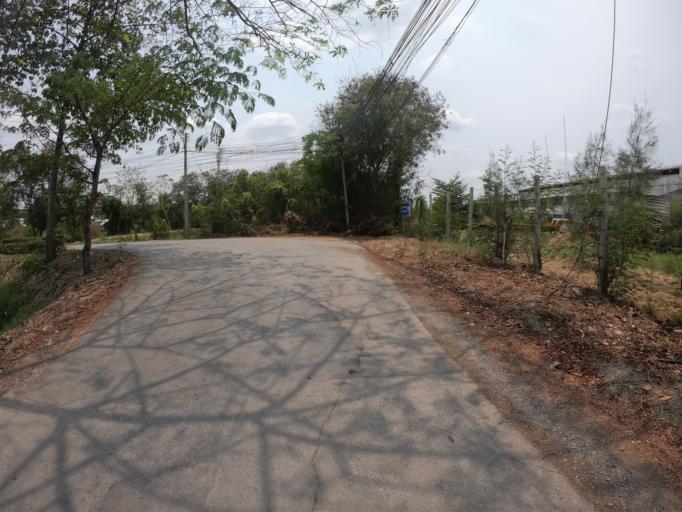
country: TH
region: Phra Nakhon Si Ayutthaya
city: Ban Bang Kadi Pathum Thani
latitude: 14.0069
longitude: 100.5696
